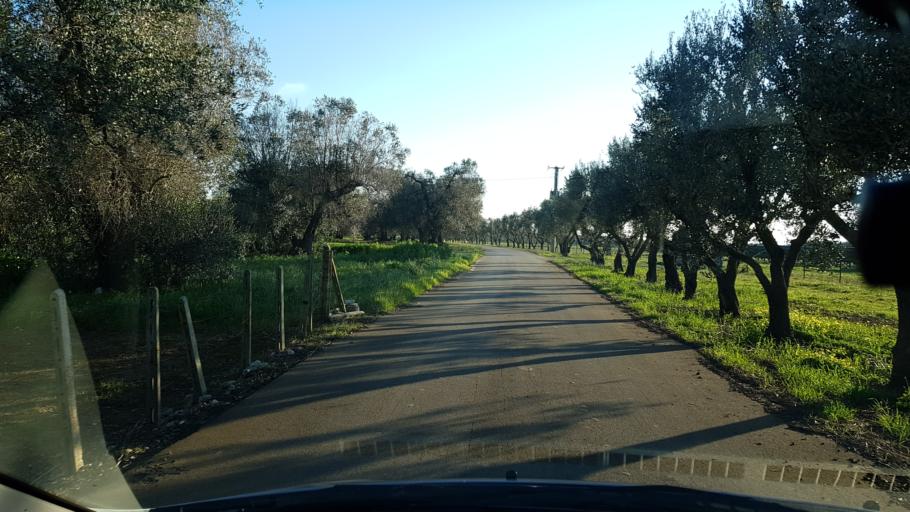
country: IT
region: Apulia
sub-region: Provincia di Brindisi
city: Mesagne
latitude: 40.5592
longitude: 17.8647
